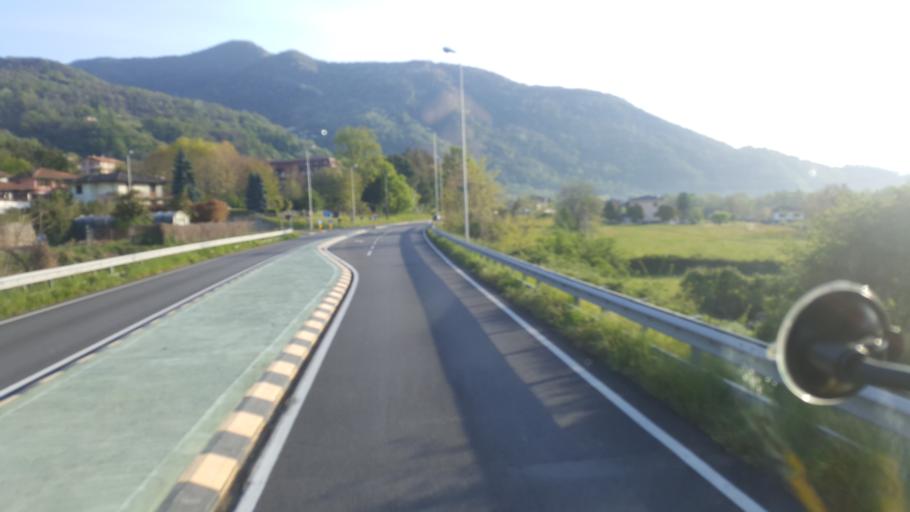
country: IT
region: Lombardy
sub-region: Provincia di Varese
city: Casalzuigno
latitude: 45.9004
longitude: 8.7058
